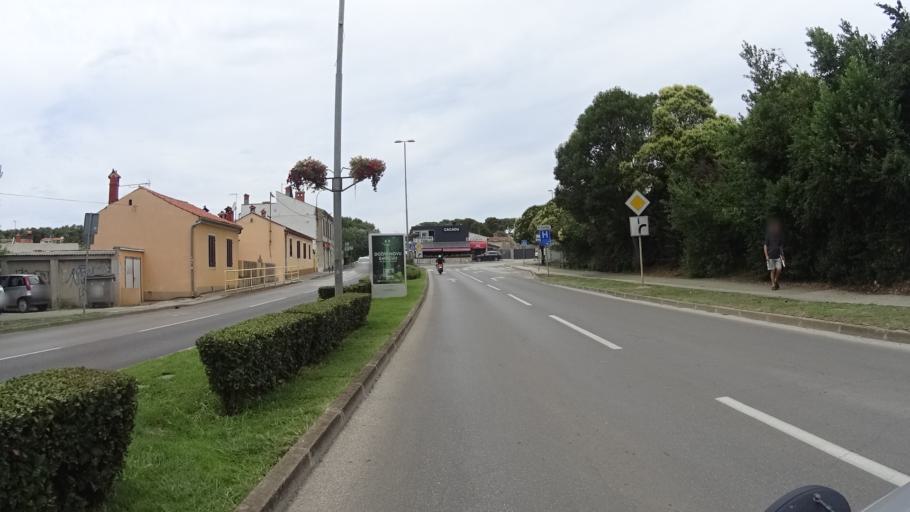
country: HR
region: Istarska
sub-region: Grad Pula
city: Pula
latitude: 44.8541
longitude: 13.8388
